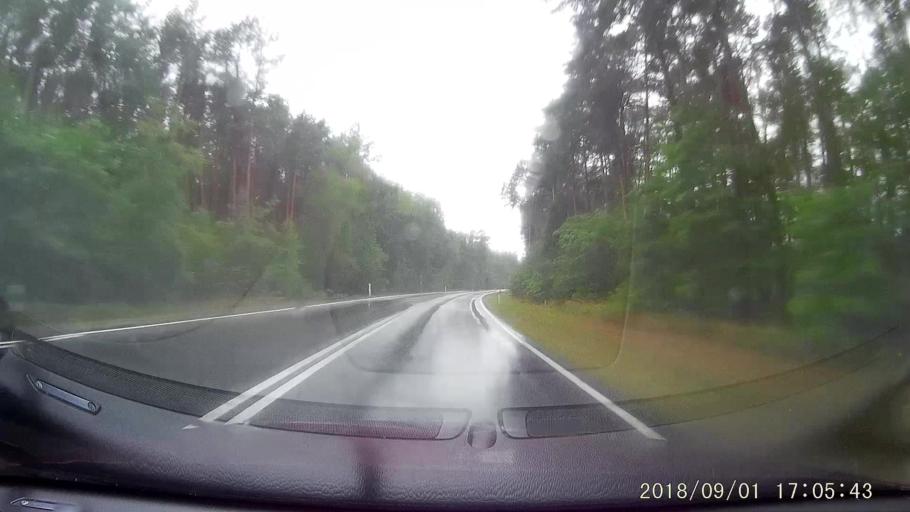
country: PL
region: Lubusz
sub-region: Powiat zielonogorski
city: Swidnica
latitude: 51.8499
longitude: 15.3502
